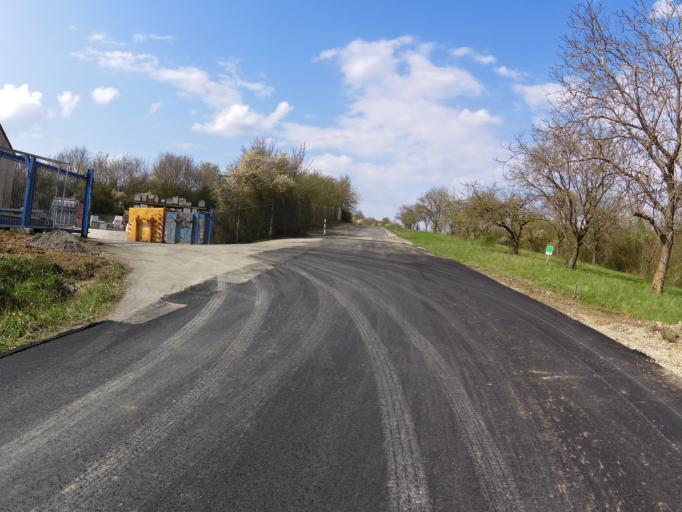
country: DE
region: Bavaria
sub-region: Regierungsbezirk Unterfranken
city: Rimpar
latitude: 49.8643
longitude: 9.9651
